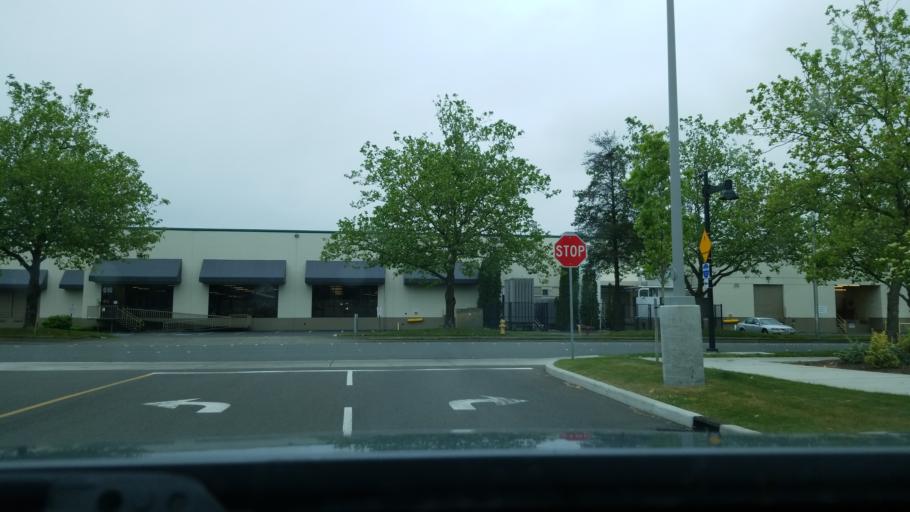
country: US
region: Washington
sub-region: King County
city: Renton
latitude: 47.4436
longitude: -122.2255
